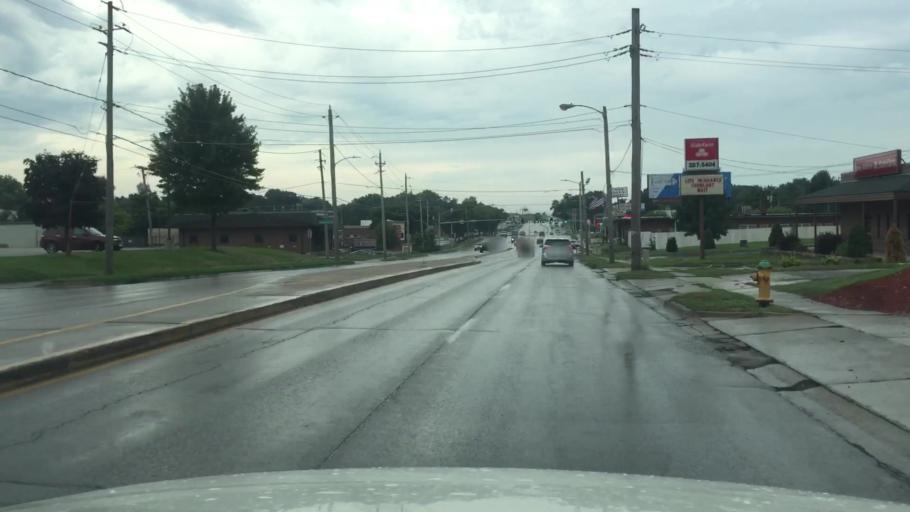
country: US
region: Iowa
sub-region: Polk County
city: Des Moines
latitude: 41.5573
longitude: -93.5970
